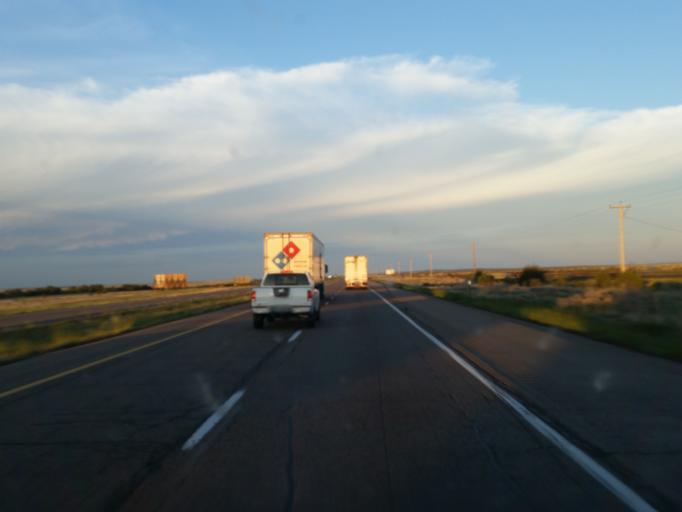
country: US
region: New Mexico
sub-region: San Miguel County
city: Las Vegas
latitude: 34.9935
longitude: -105.3394
